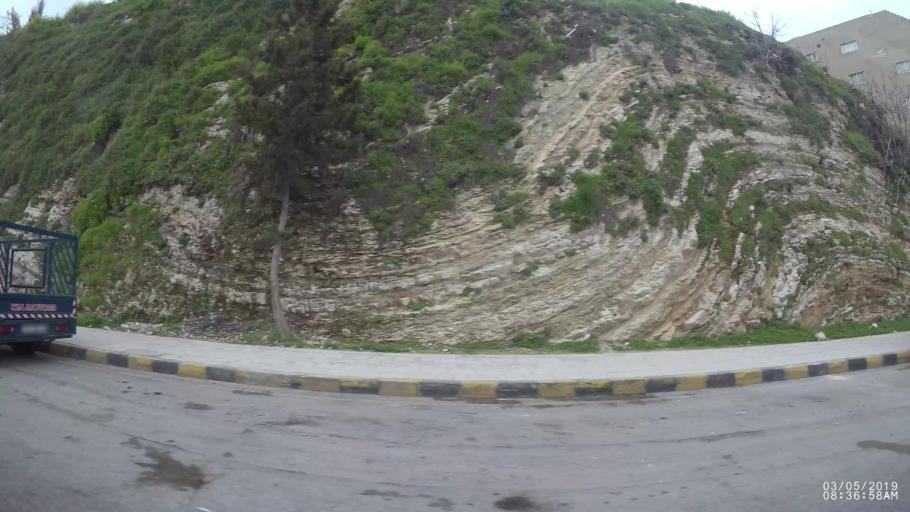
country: JO
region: Amman
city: Amman
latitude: 31.9572
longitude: 35.9362
